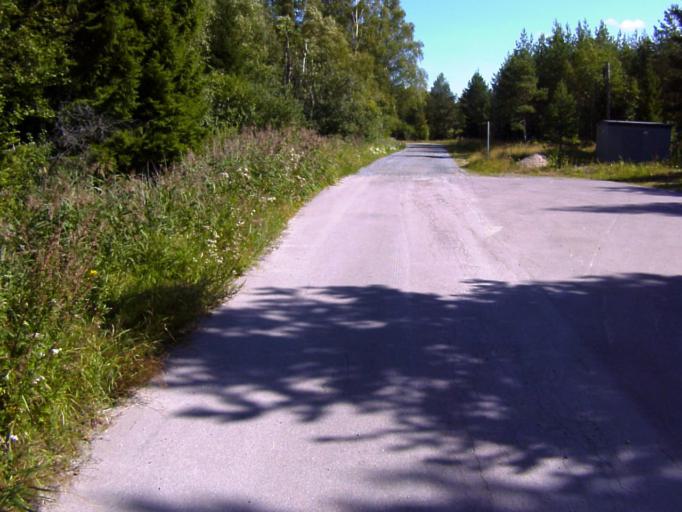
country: SE
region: Soedermanland
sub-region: Eskilstuna Kommun
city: Eskilstuna
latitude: 59.3487
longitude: 16.5722
